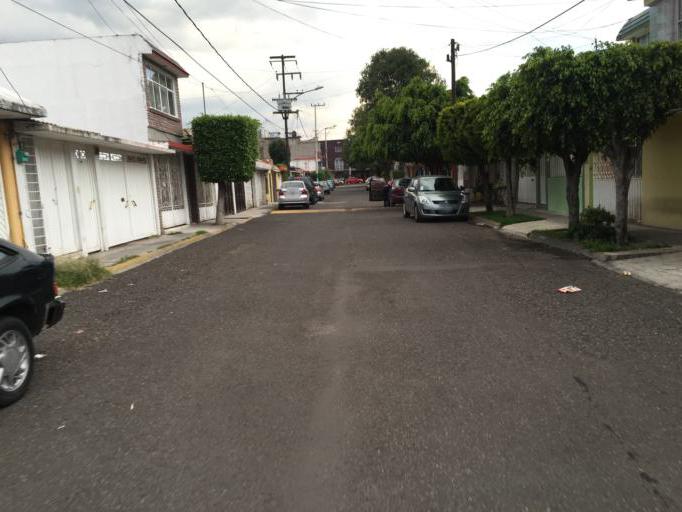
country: MX
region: Mexico
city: Cuautitlan Izcalli
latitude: 19.6544
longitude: -99.2105
